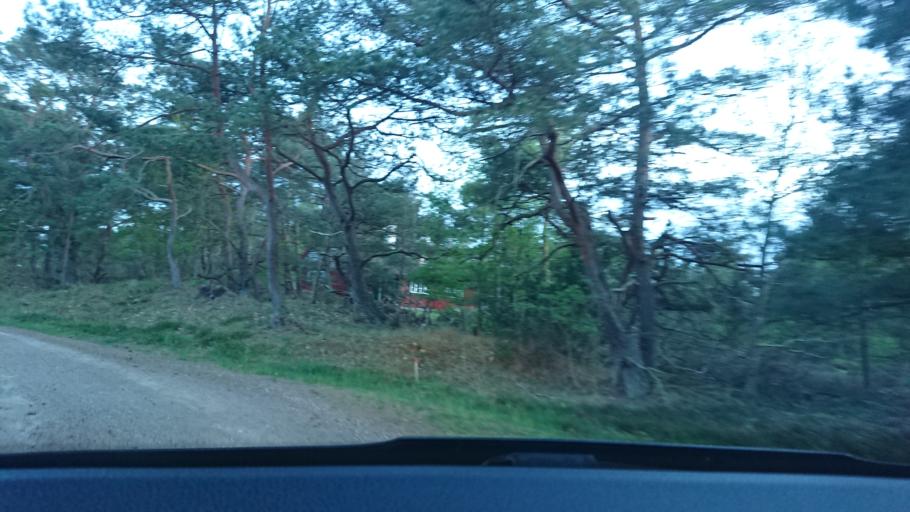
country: DK
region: Zealand
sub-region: Odsherred Kommune
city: Nykobing Sjaelland
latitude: 55.9445
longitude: 11.6974
